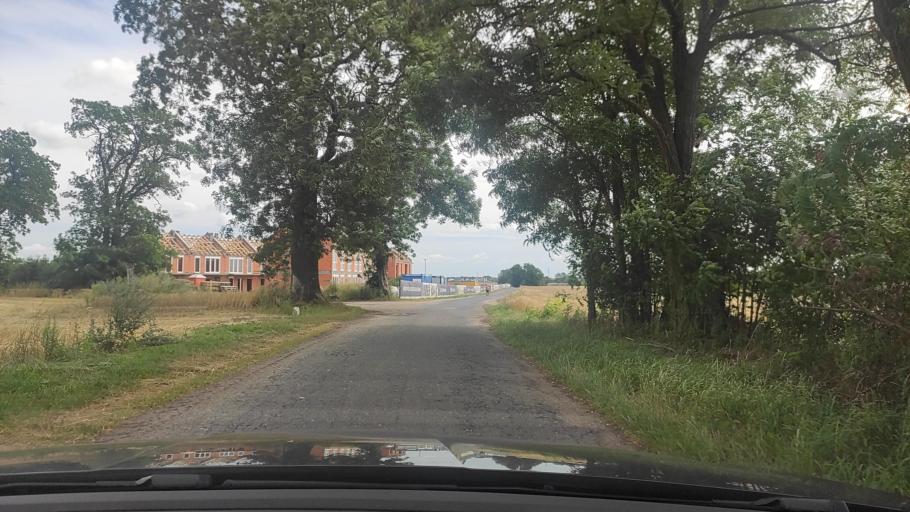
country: PL
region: Greater Poland Voivodeship
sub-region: Powiat poznanski
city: Kostrzyn
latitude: 52.4089
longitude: 17.1885
